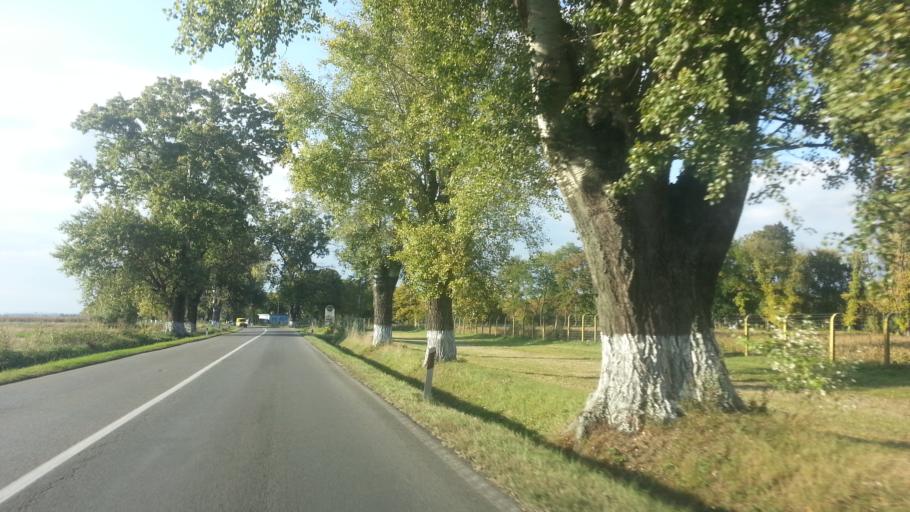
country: RS
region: Autonomna Pokrajina Vojvodina
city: Nova Pazova
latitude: 44.9245
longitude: 20.2475
